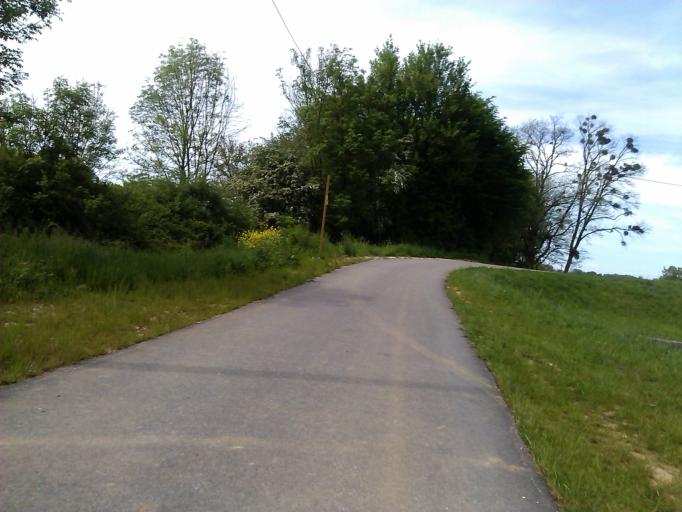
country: FR
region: Franche-Comte
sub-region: Departement du Doubs
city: Boussieres
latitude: 47.1554
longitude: 5.8561
